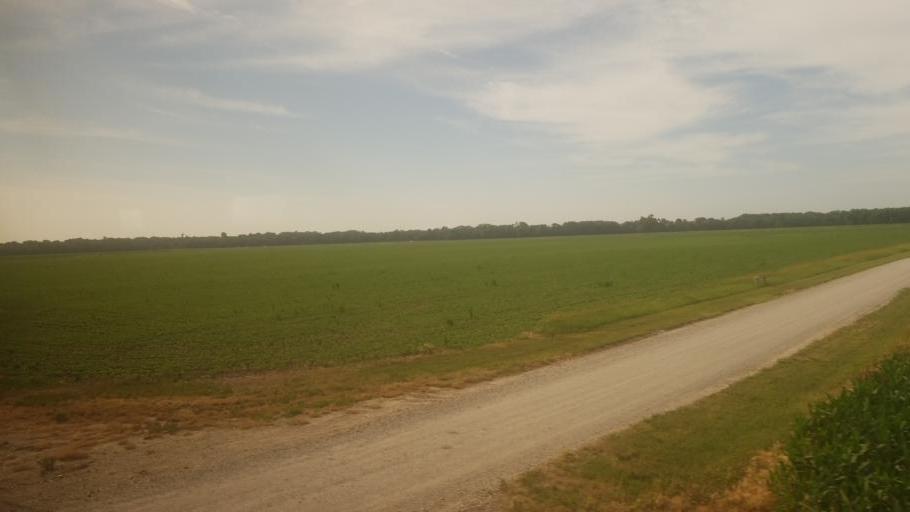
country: US
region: Kansas
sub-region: Douglas County
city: Eudora
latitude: 38.9497
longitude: -95.1304
